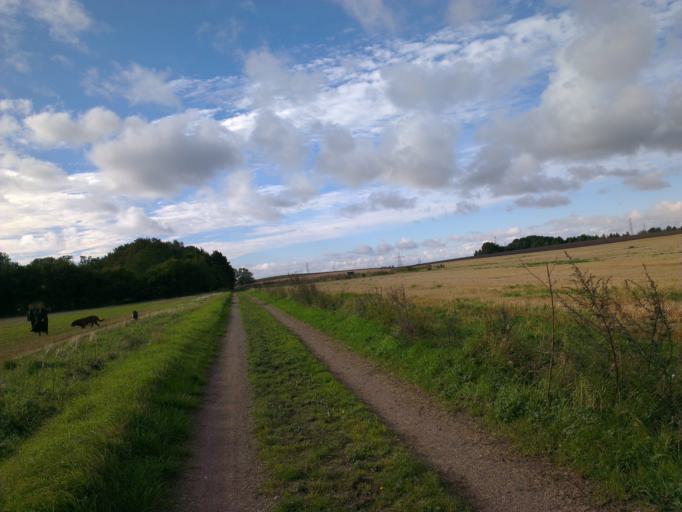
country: DK
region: Capital Region
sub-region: Frederikssund Kommune
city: Frederikssund
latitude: 55.8027
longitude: 12.0879
